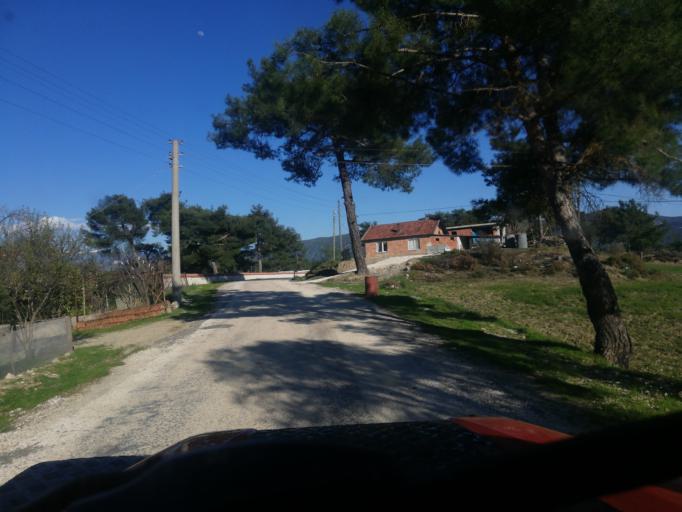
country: TR
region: Antalya
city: Kas
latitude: 36.2983
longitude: 29.6977
